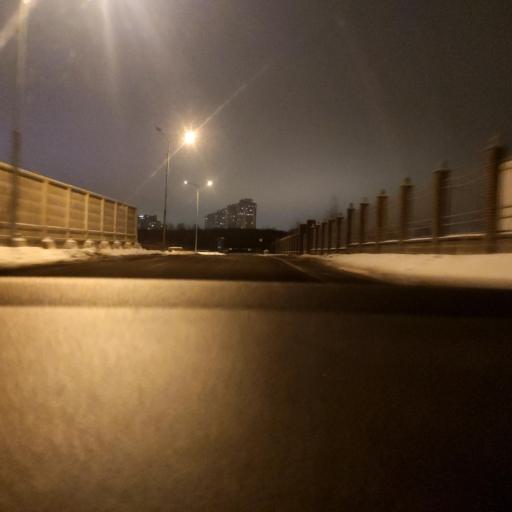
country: RU
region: Moskovskaya
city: Vostryakovo
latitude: 55.6587
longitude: 37.4551
